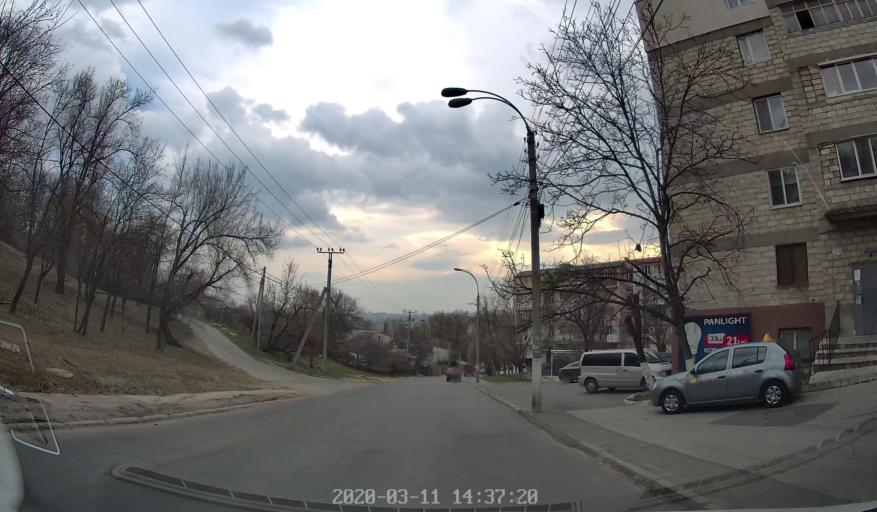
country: MD
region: Chisinau
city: Chisinau
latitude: 47.0224
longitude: 28.8755
